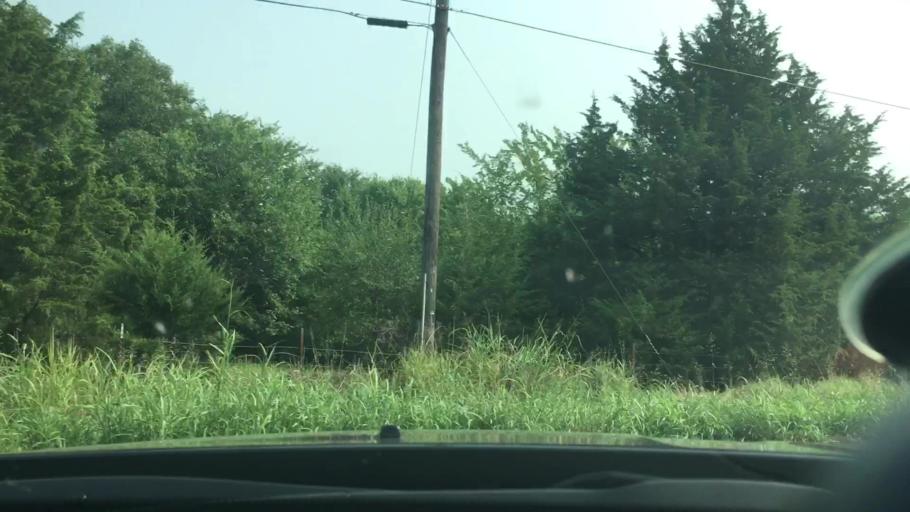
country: US
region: Oklahoma
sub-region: Garvin County
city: Lindsay
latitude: 34.8120
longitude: -97.6429
